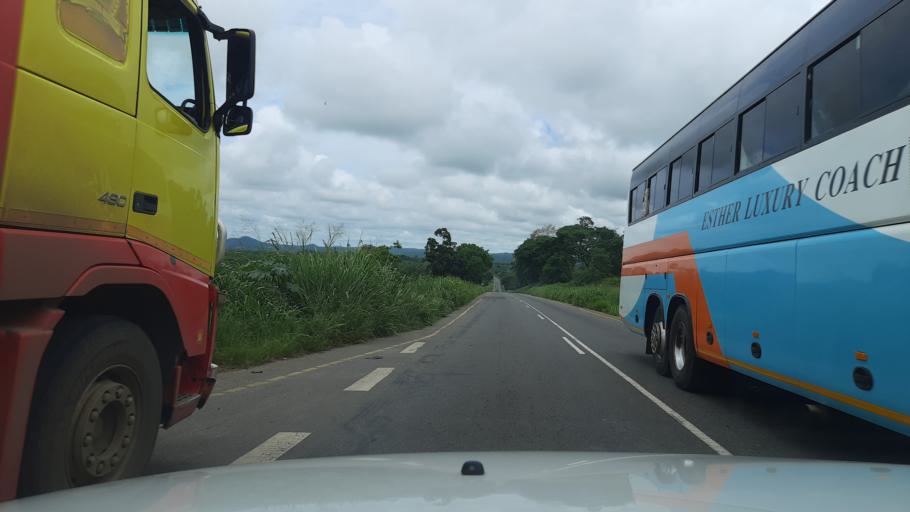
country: TZ
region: Pwani
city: Lugoba
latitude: -5.9606
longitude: 38.2240
